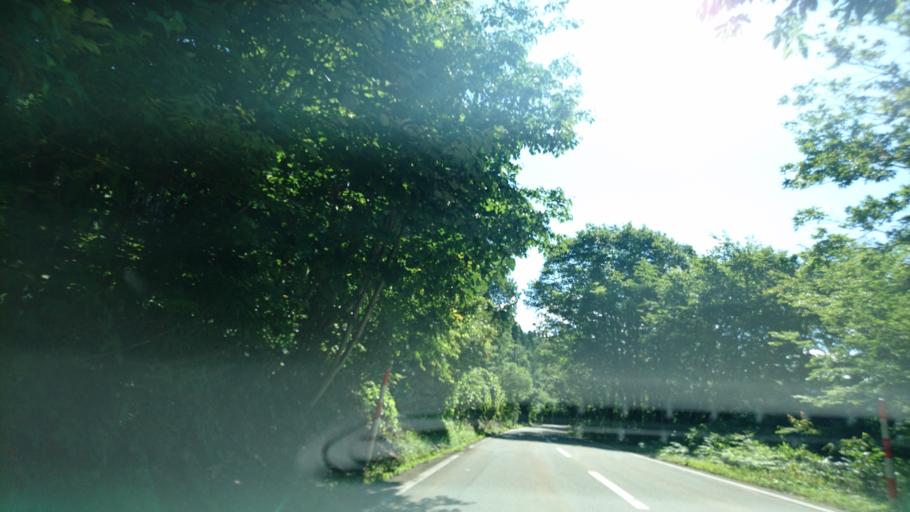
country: JP
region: Akita
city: Kakunodatemachi
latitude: 39.7485
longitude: 140.6727
